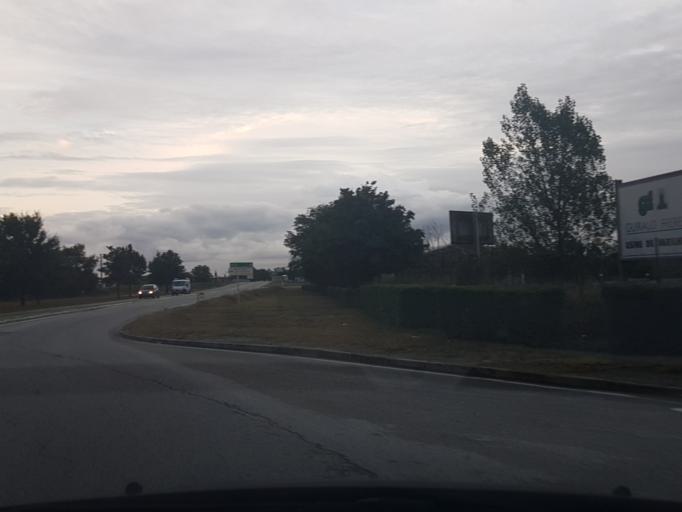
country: FR
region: Midi-Pyrenees
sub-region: Departement de l'Ariege
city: Verniolle
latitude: 43.0686
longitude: 1.6405
